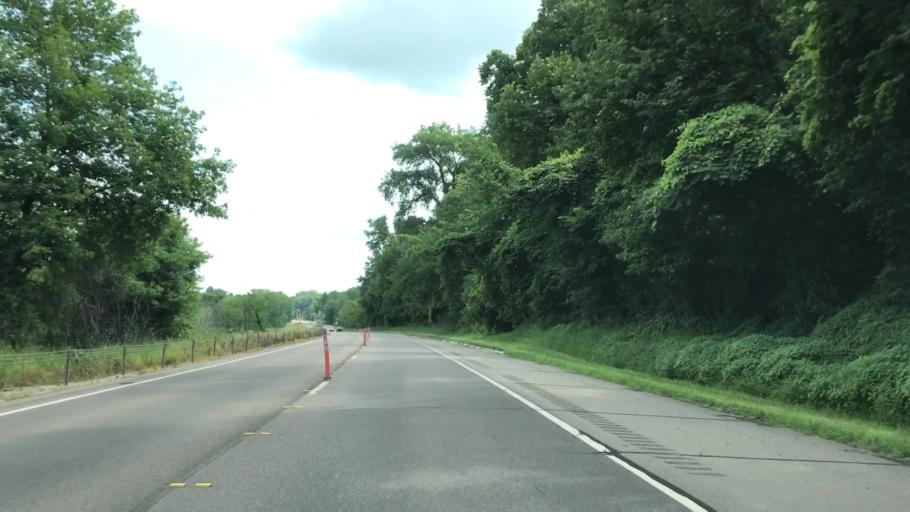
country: US
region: Minnesota
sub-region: Nicollet County
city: Saint Peter
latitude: 44.3762
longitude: -93.9685
